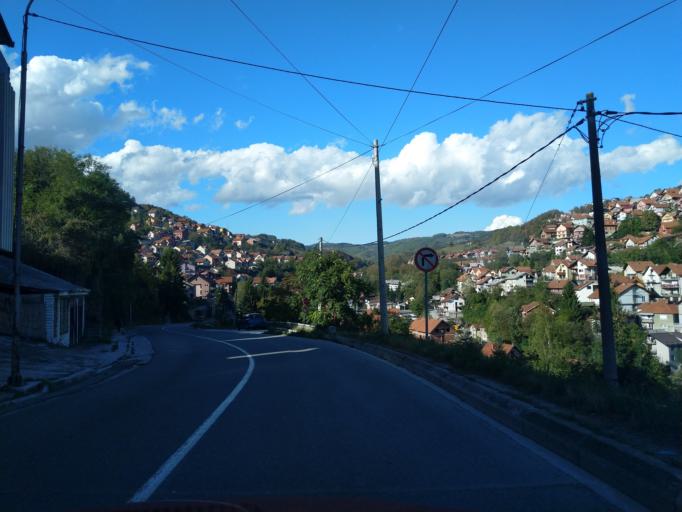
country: RS
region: Central Serbia
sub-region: Zlatiborski Okrug
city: Uzice
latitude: 43.8598
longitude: 19.8258
